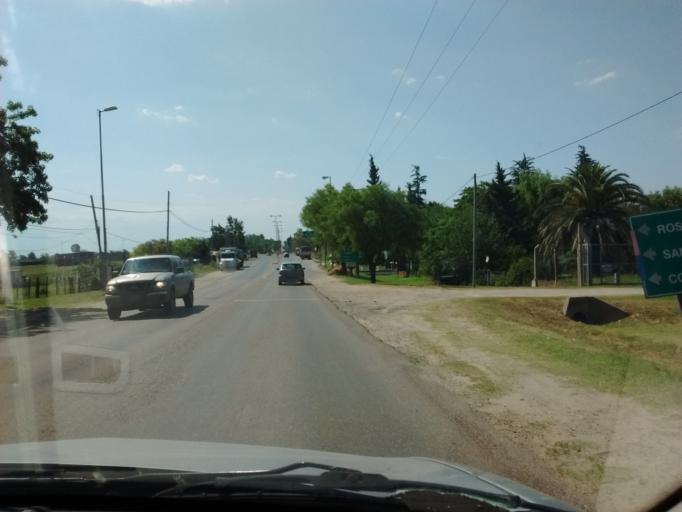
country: AR
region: Entre Rios
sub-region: Departamento de Victoria
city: Victoria
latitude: -32.6081
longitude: -60.1664
